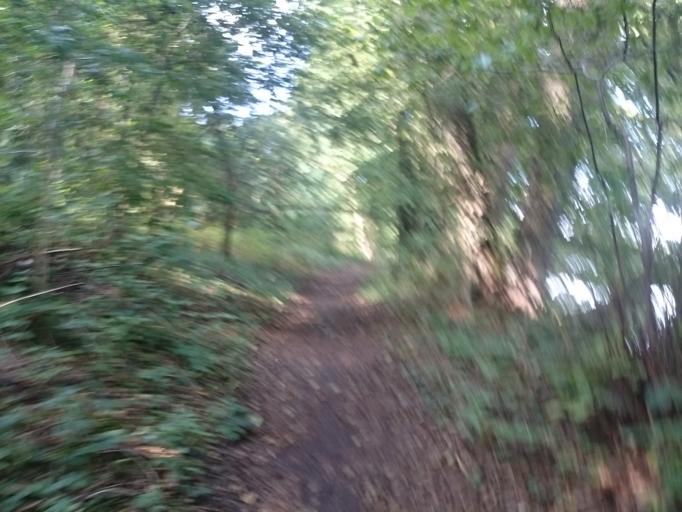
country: DE
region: Brandenburg
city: Lychen
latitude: 53.3037
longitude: 13.4247
